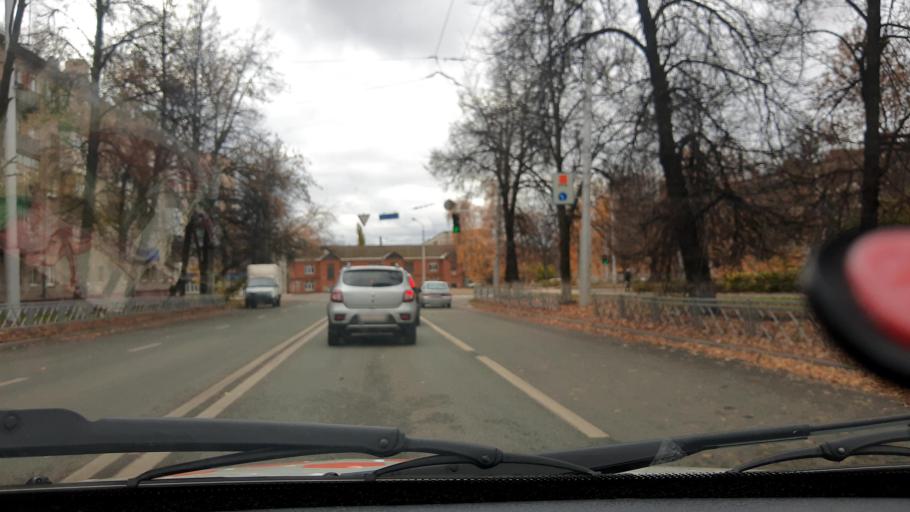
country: RU
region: Bashkortostan
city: Ufa
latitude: 54.8157
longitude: 56.1046
